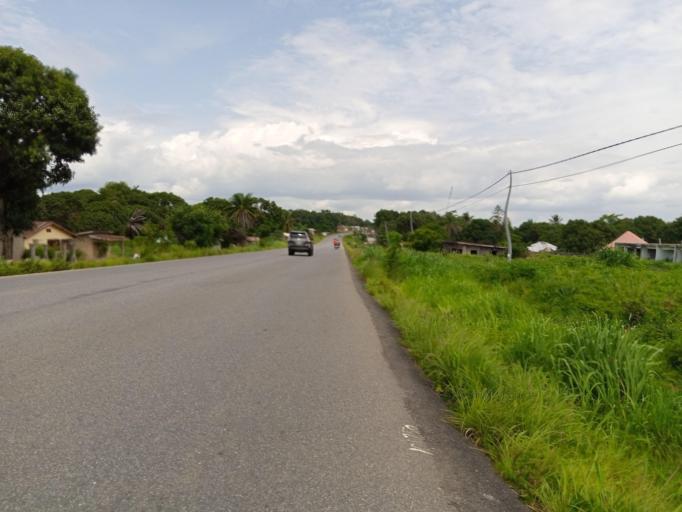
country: SL
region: Northern Province
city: Masoyila
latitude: 8.5432
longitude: -13.1535
